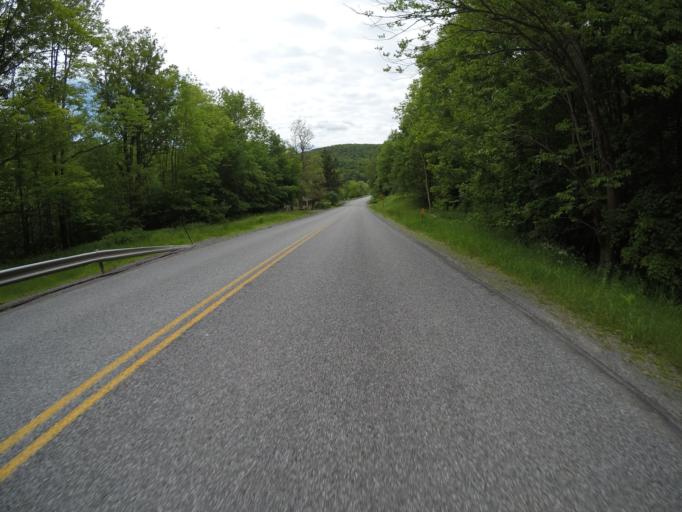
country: US
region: New York
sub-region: Delaware County
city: Stamford
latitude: 42.1865
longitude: -74.5851
